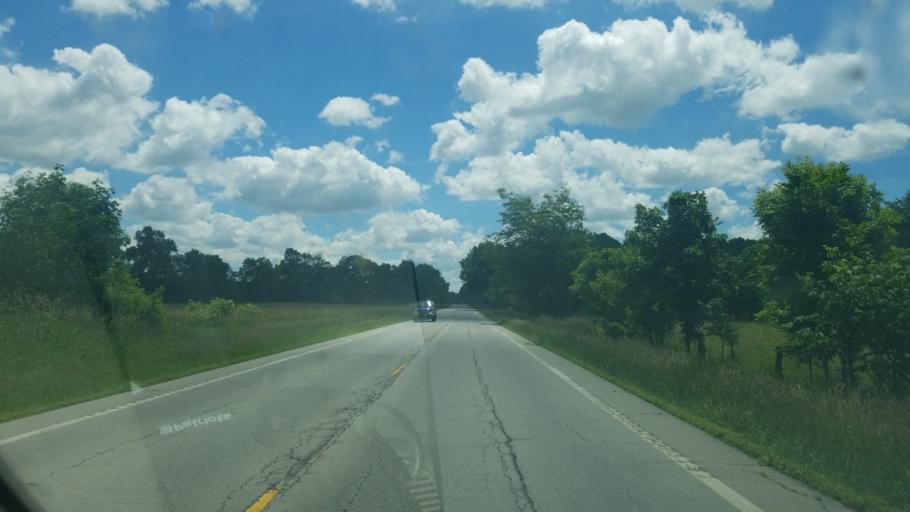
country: US
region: Ohio
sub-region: Huron County
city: New London
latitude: 41.0430
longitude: -82.4307
